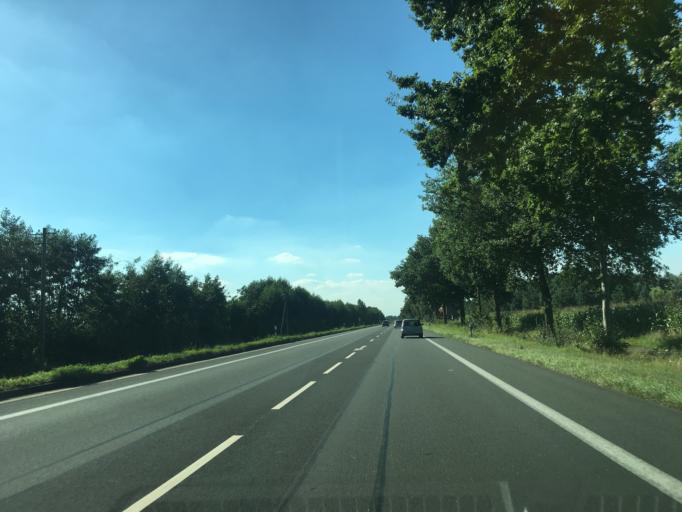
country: DE
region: North Rhine-Westphalia
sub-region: Regierungsbezirk Munster
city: Beelen
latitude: 51.9178
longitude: 8.1532
